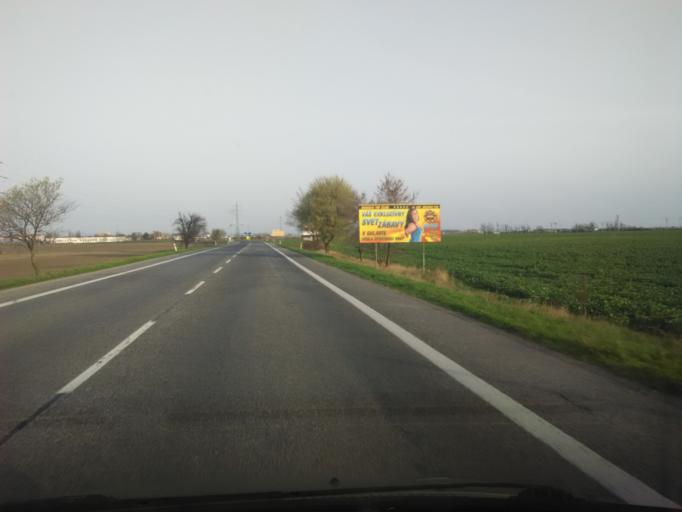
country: SK
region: Trnavsky
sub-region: Okres Galanta
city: Galanta
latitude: 48.1881
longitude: 17.7570
